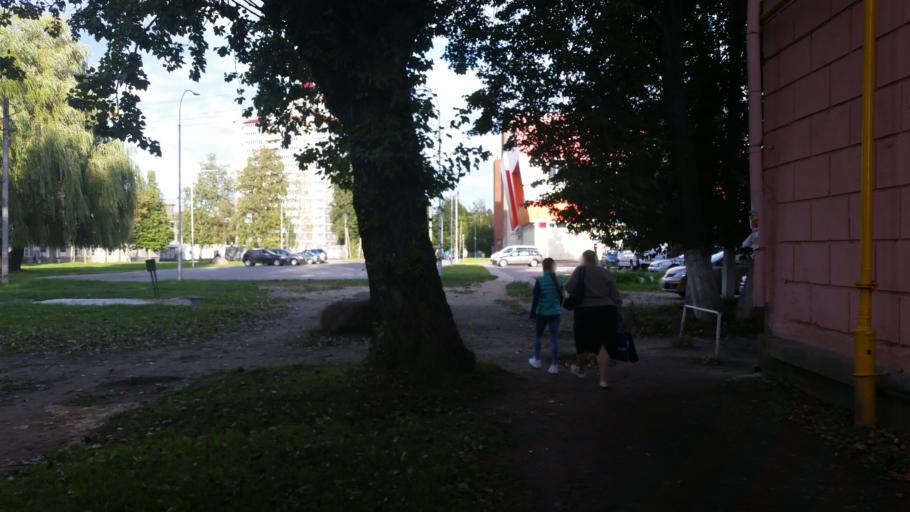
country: BY
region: Vitebsk
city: Vitebsk
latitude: 55.1831
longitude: 30.1899
